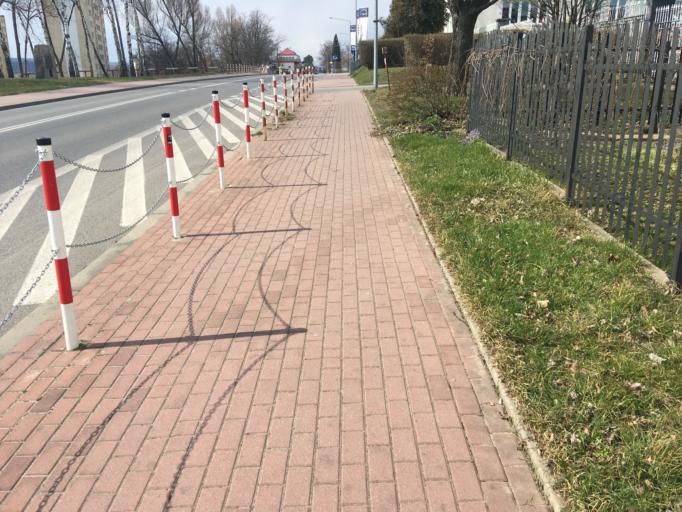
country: PL
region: Swietokrzyskie
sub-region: Powiat starachowicki
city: Starachowice
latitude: 51.0544
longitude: 21.0626
